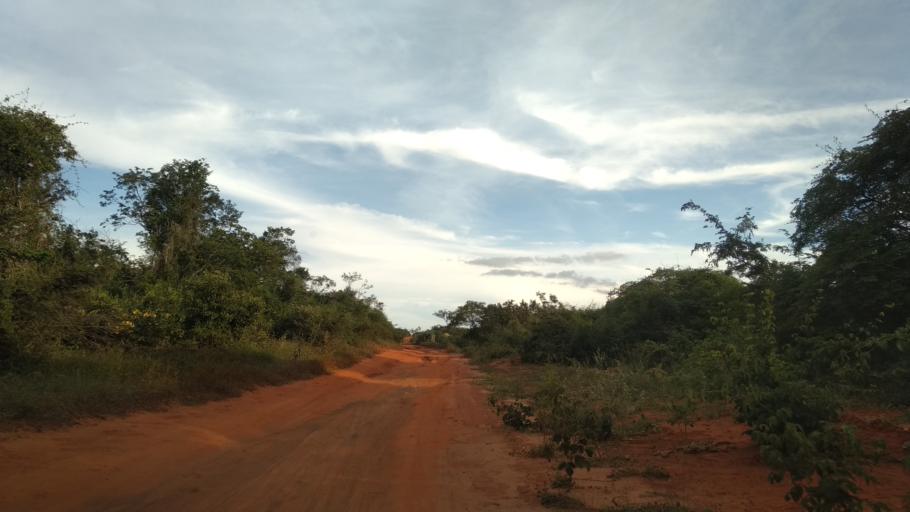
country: BR
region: Bahia
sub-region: Caetite
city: Caetite
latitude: -13.9824
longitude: -42.5109
